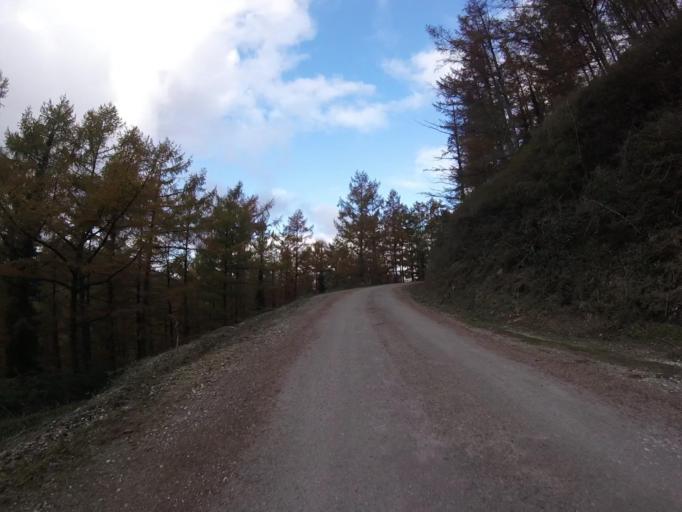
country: ES
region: Navarre
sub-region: Provincia de Navarra
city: Arano
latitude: 43.2131
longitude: -1.8575
